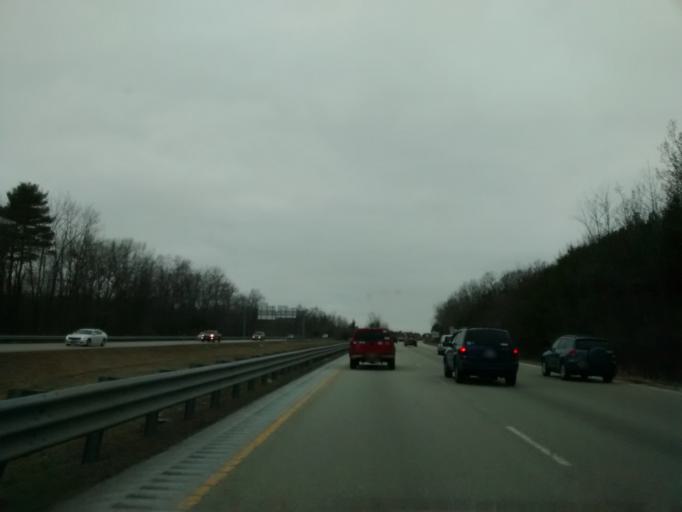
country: US
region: Massachusetts
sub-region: Worcester County
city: Westminster
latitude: 42.5457
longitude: -71.9025
